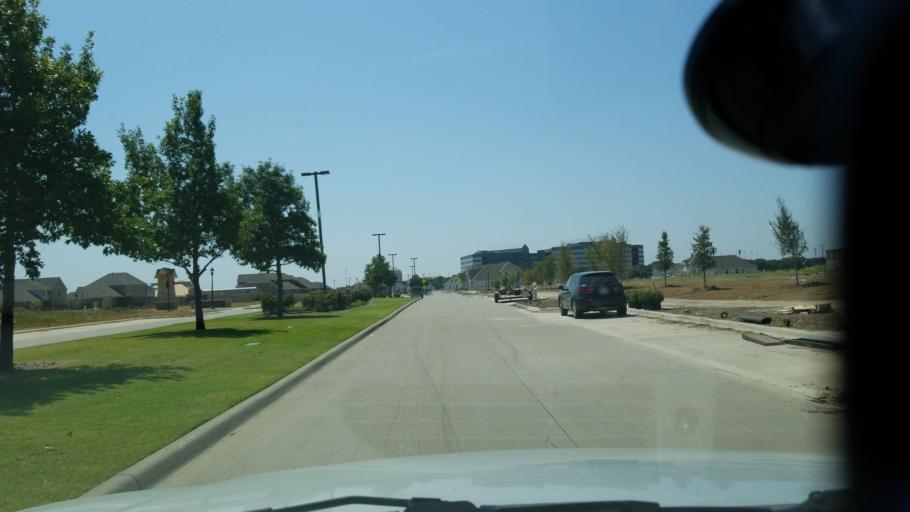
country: US
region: Texas
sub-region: Dallas County
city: Farmers Branch
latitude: 32.9152
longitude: -96.9301
